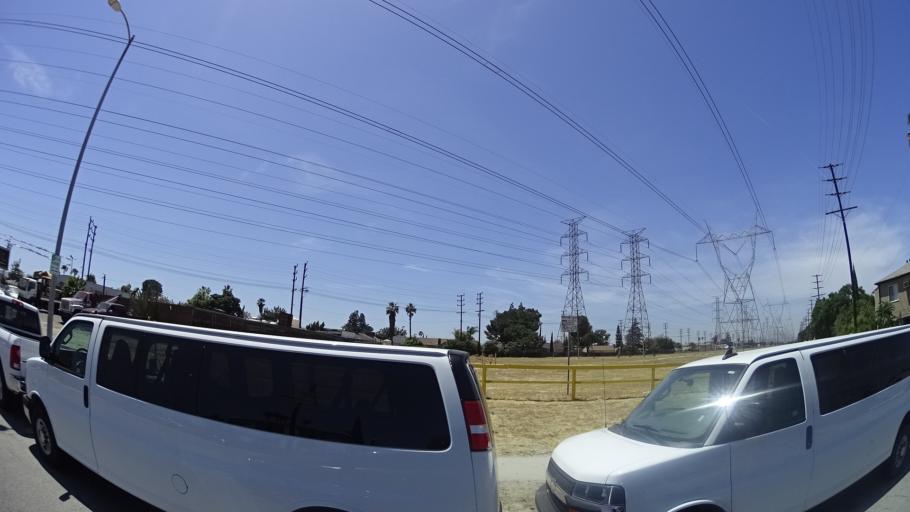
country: US
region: California
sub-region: Los Angeles County
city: North Hollywood
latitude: 34.1840
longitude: -118.3704
